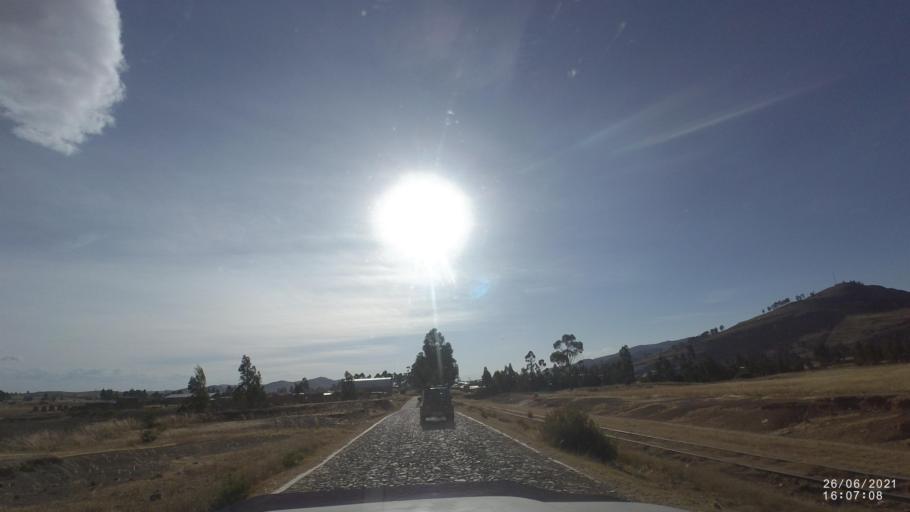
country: BO
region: Cochabamba
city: Arani
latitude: -17.8216
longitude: -65.7730
